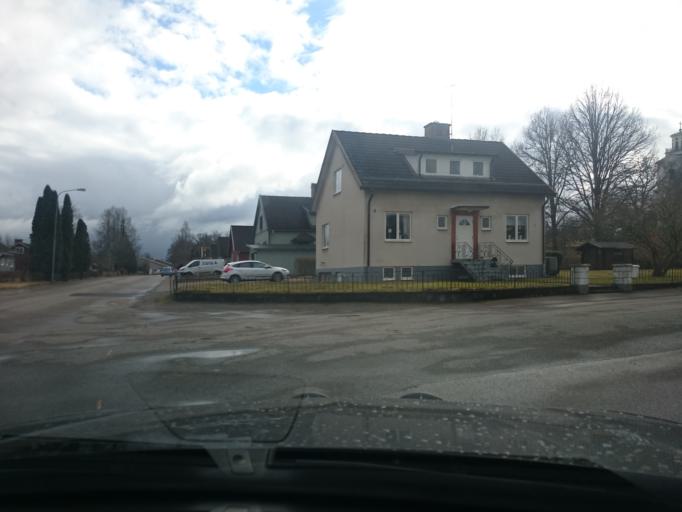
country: SE
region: Joenkoeping
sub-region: Vetlanda Kommun
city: Vetlanda
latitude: 57.3080
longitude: 15.1260
